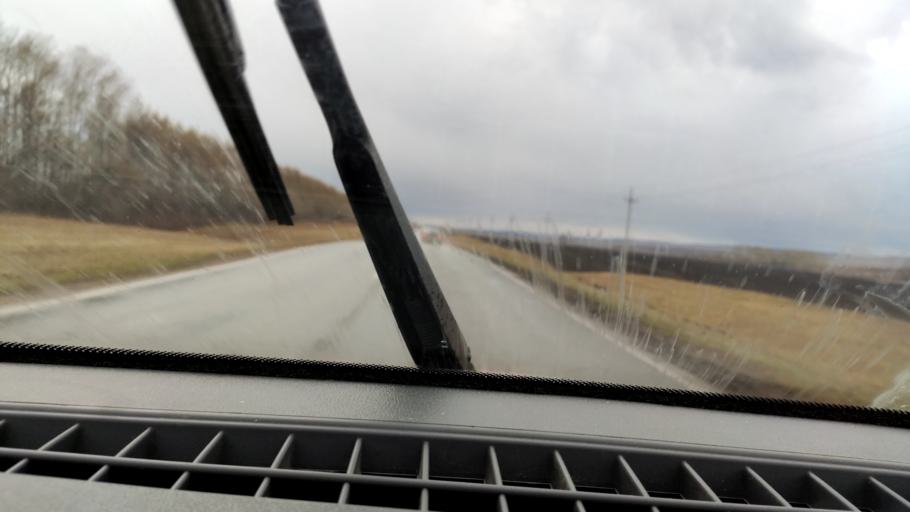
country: RU
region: Bashkortostan
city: Chekmagush
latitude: 55.1114
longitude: 54.9155
